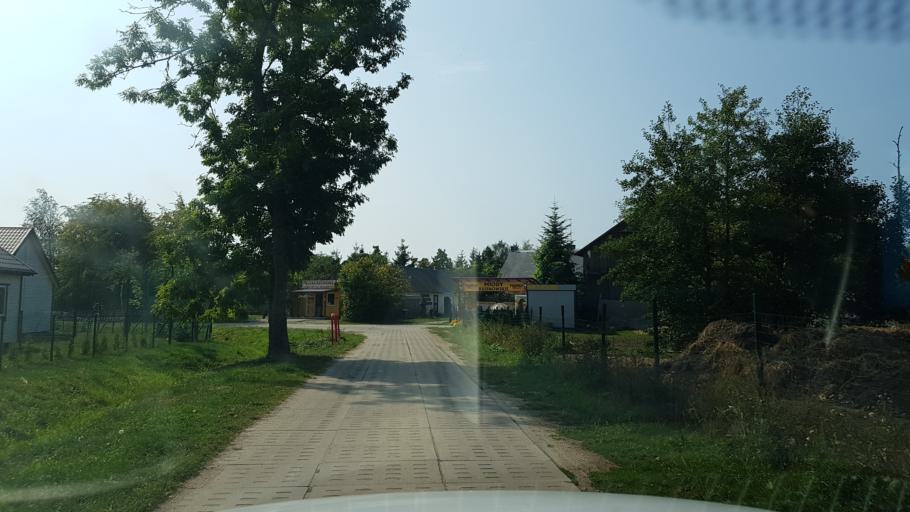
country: PL
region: West Pomeranian Voivodeship
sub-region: Powiat slawienski
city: Darlowo
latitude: 54.5076
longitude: 16.4998
